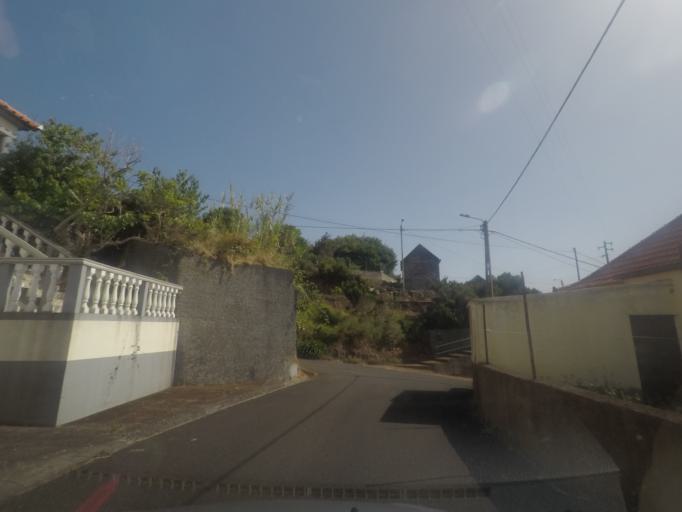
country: PT
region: Madeira
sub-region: Calheta
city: Faja da Ovelha
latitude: 32.8267
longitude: -17.2336
